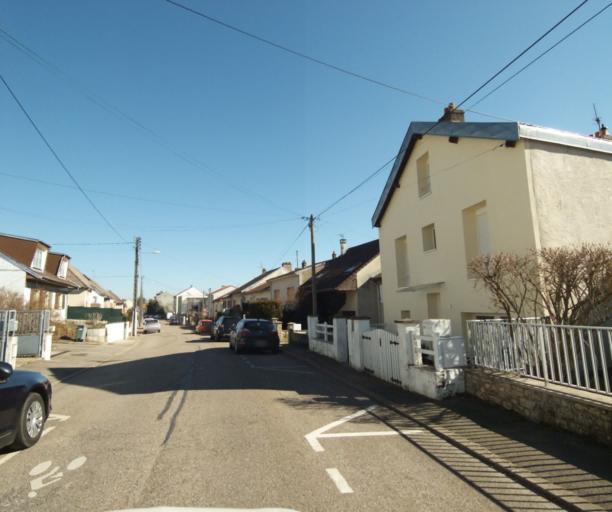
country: FR
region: Lorraine
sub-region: Departement de Meurthe-et-Moselle
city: Essey-les-Nancy
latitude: 48.7068
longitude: 6.2301
